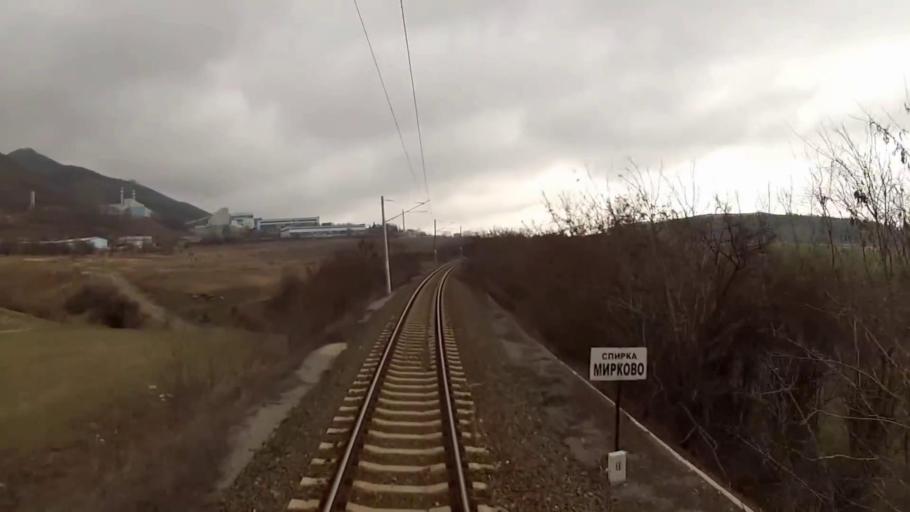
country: BG
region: Sofiya
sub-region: Obshtina Mirkovo
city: Mirkovo
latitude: 42.6952
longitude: 24.0164
